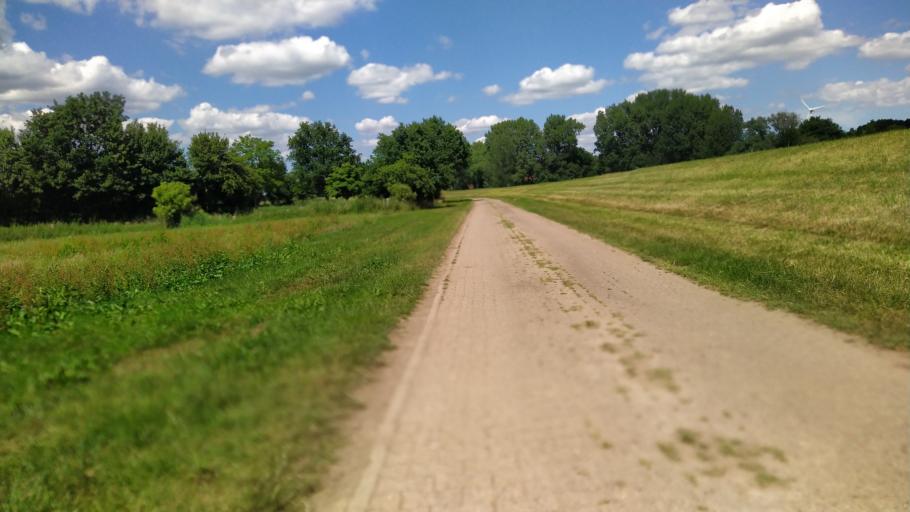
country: DE
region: Lower Saxony
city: Estorf
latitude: 53.5708
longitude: 9.1683
